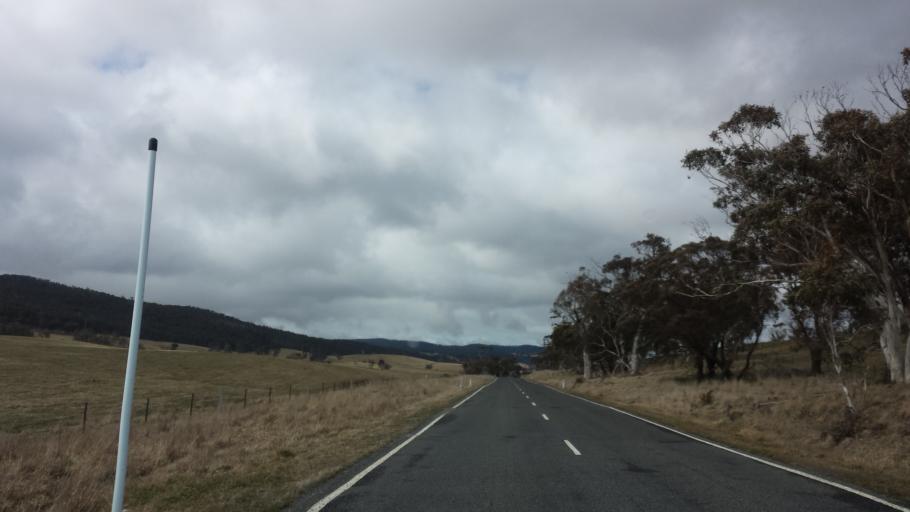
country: AU
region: Victoria
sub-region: Alpine
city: Mount Beauty
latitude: -37.1232
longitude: 147.4481
